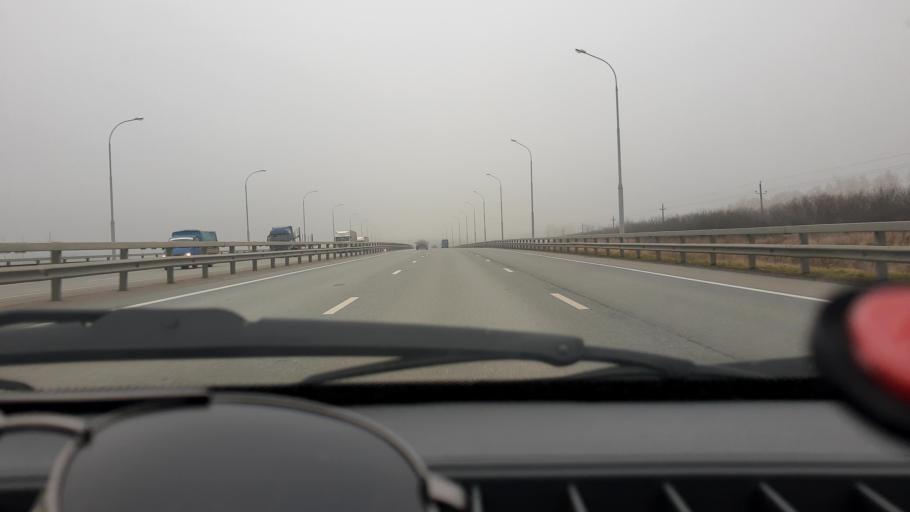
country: RU
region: Bashkortostan
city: Kabakovo
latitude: 54.6597
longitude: 56.1357
